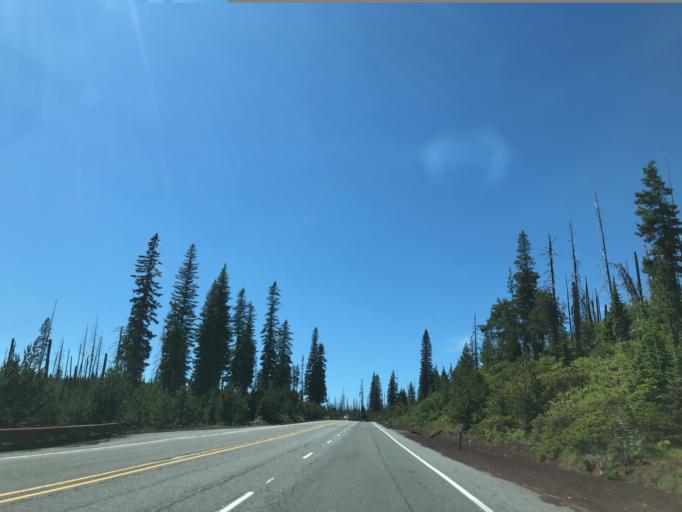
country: US
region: Oregon
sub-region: Deschutes County
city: Sisters
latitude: 44.4241
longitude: -121.8358
